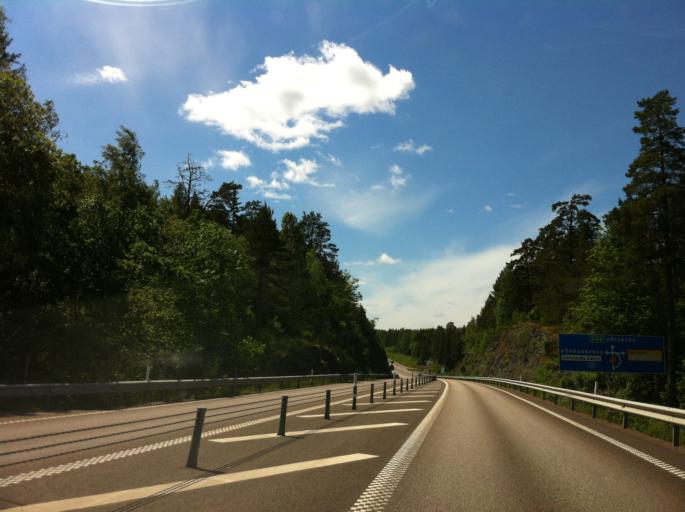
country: SE
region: Vaestra Goetaland
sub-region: Melleruds Kommun
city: Mellerud
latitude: 58.7774
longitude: 12.5020
